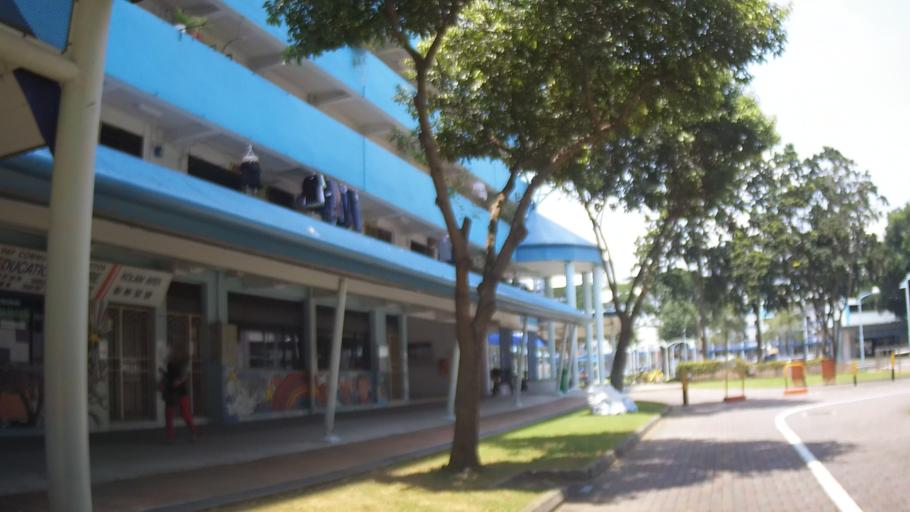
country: SG
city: Singapore
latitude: 1.3203
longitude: 103.8686
